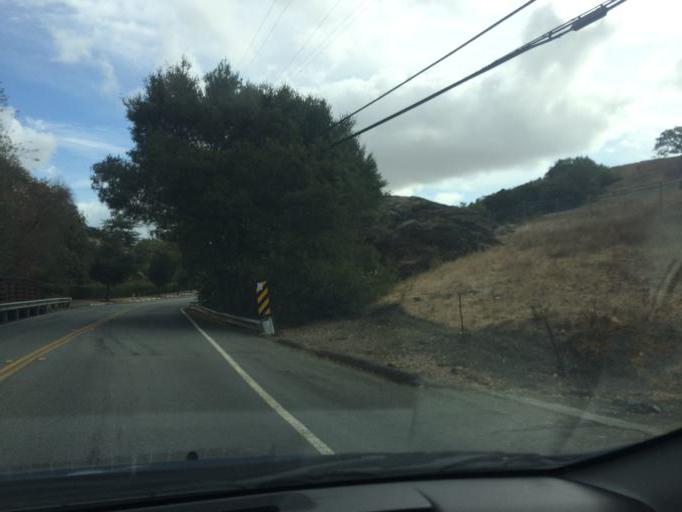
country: US
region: California
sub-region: Santa Clara County
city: Seven Trees
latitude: 37.2775
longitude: -121.7494
